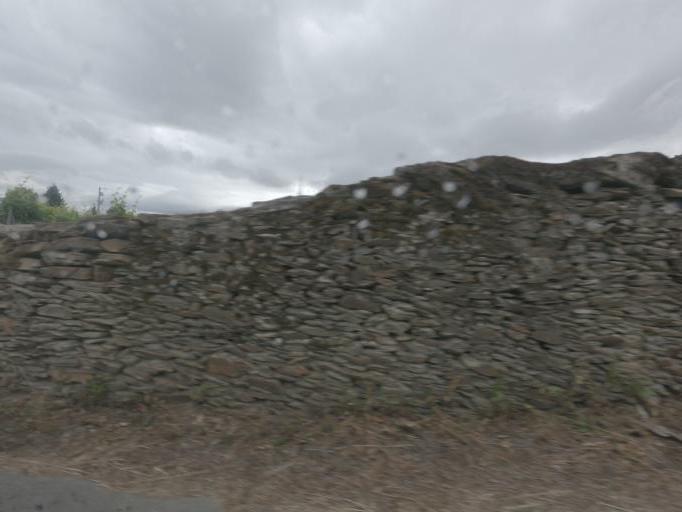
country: PT
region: Vila Real
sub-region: Sabrosa
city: Sabrosa
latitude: 41.2516
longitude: -7.4963
